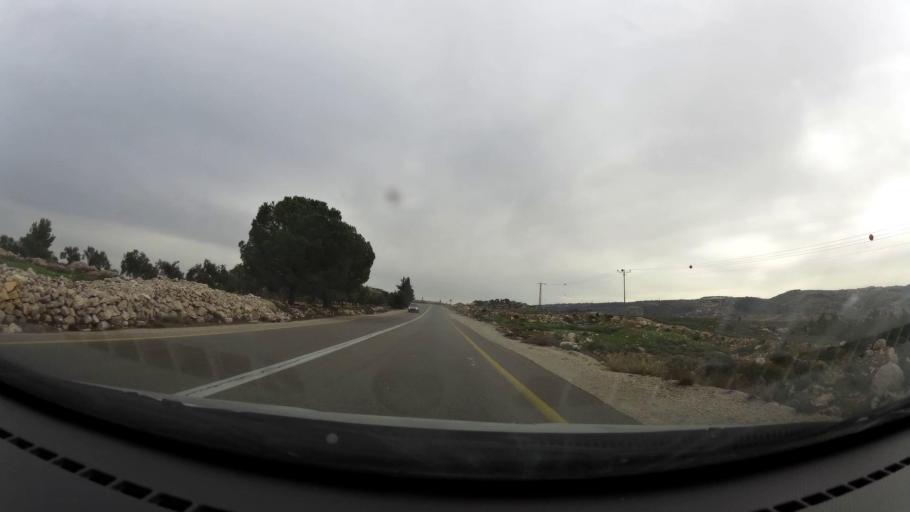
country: PS
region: West Bank
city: Surif
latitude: 31.6722
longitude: 35.0652
